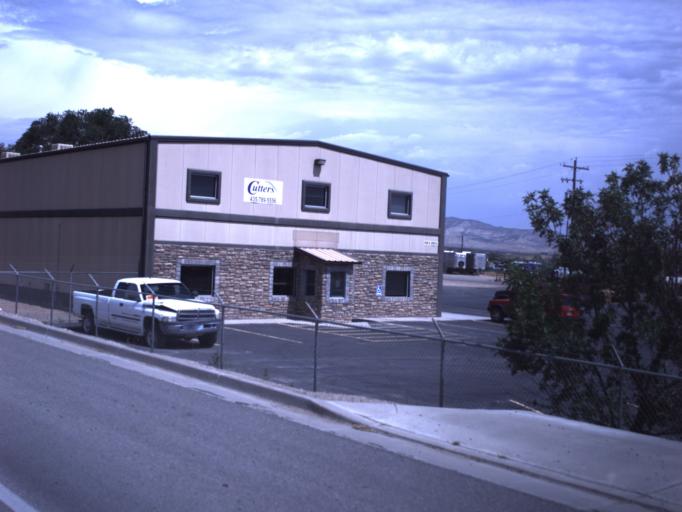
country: US
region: Utah
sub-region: Uintah County
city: Naples
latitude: 40.4462
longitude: -109.5004
